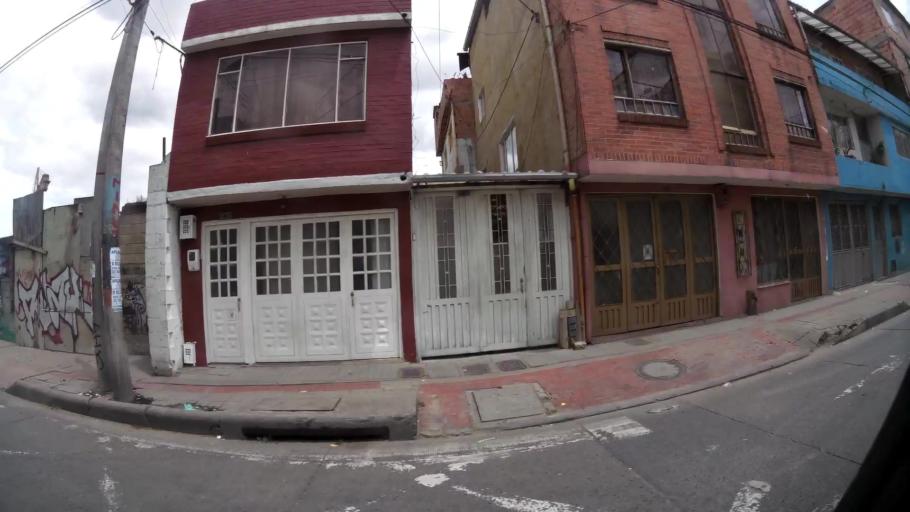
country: CO
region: Cundinamarca
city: Funza
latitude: 4.7048
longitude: -74.1325
